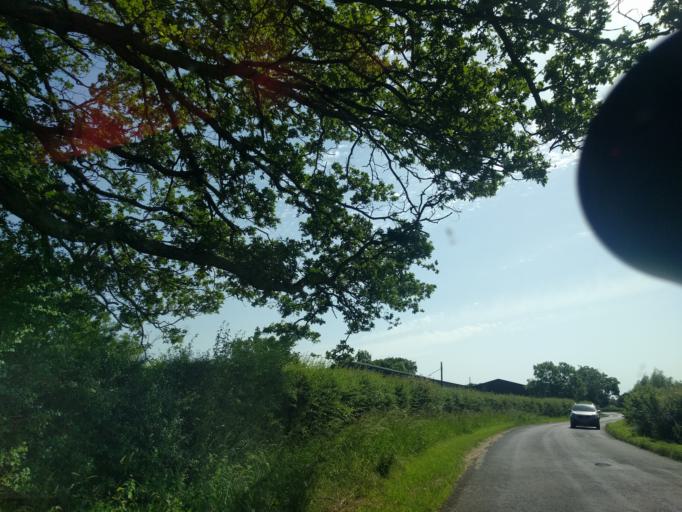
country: GB
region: England
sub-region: Wiltshire
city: Lyneham
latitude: 51.5344
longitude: -1.9820
